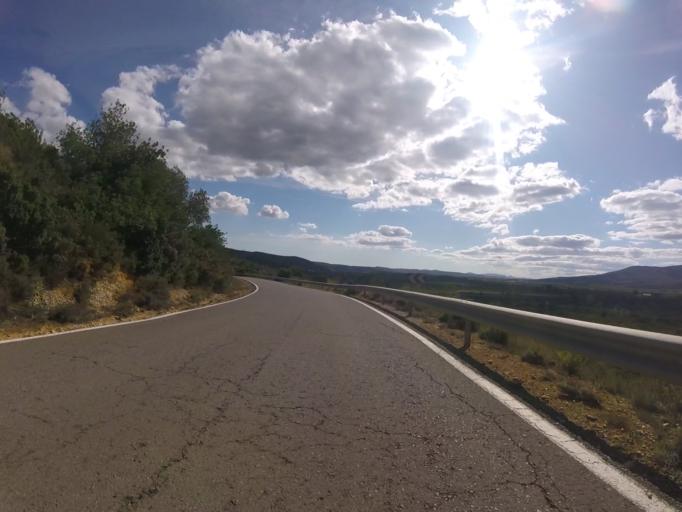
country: ES
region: Valencia
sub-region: Provincia de Castello
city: Cuevas de Vinroma
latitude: 40.3692
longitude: 0.1181
